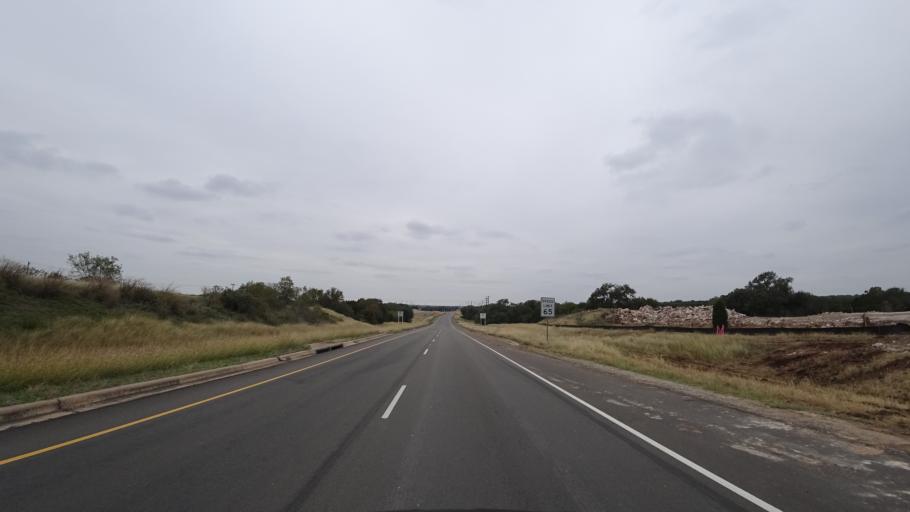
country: US
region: Texas
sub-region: Travis County
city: Shady Hollow
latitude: 30.1900
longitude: -97.8755
